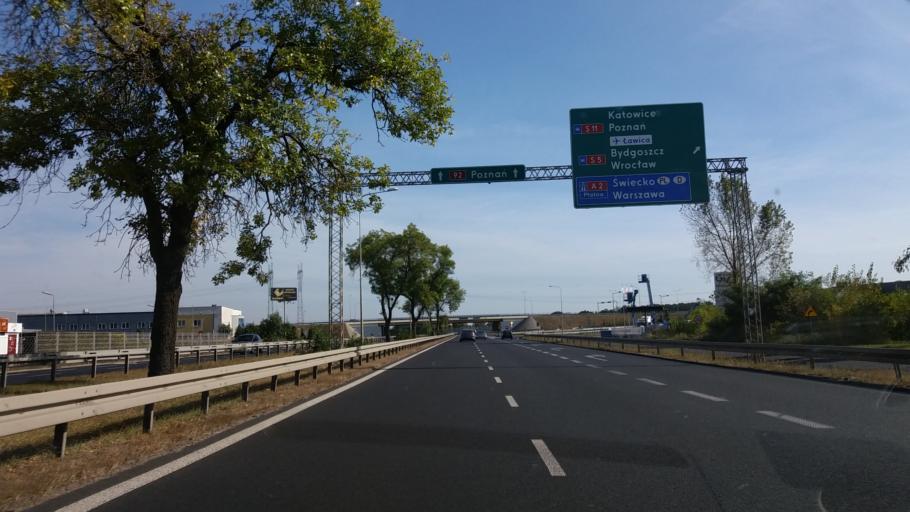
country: PL
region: Greater Poland Voivodeship
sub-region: Powiat poznanski
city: Baranowo
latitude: 52.4443
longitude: 16.7364
